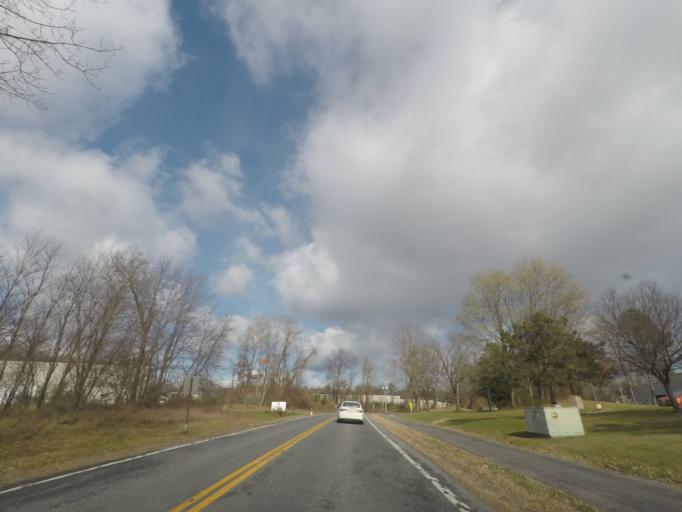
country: US
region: New York
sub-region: Saratoga County
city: Country Knolls
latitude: 42.8987
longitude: -73.7940
